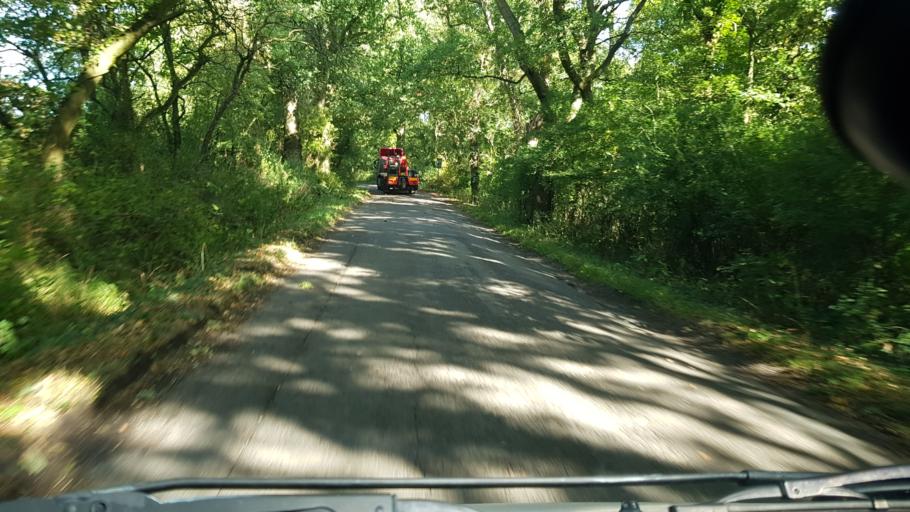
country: GB
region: England
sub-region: Surrey
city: Shalford
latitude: 51.2106
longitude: -0.5959
